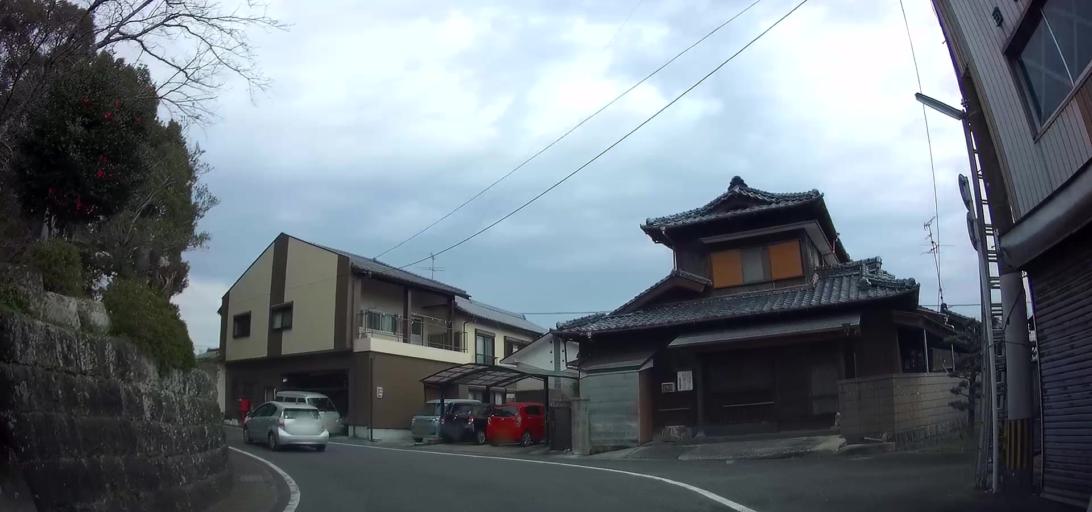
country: JP
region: Nagasaki
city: Shimabara
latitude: 32.6738
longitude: 130.3019
